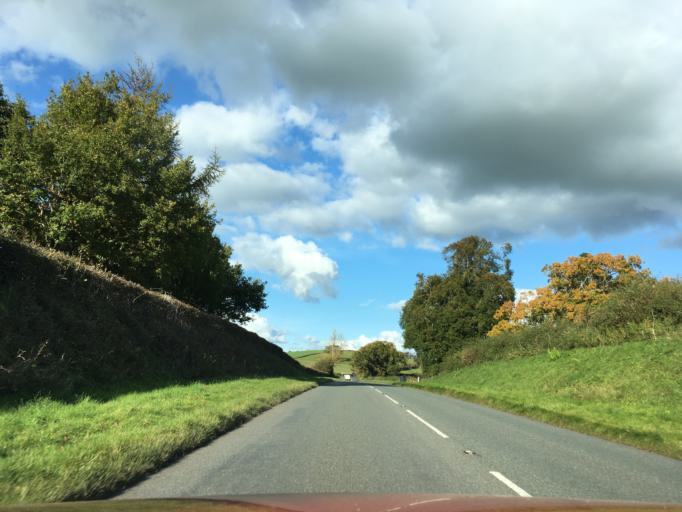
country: GB
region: Wales
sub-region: Sir Powys
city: Brecon
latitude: 51.9562
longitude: -3.3791
